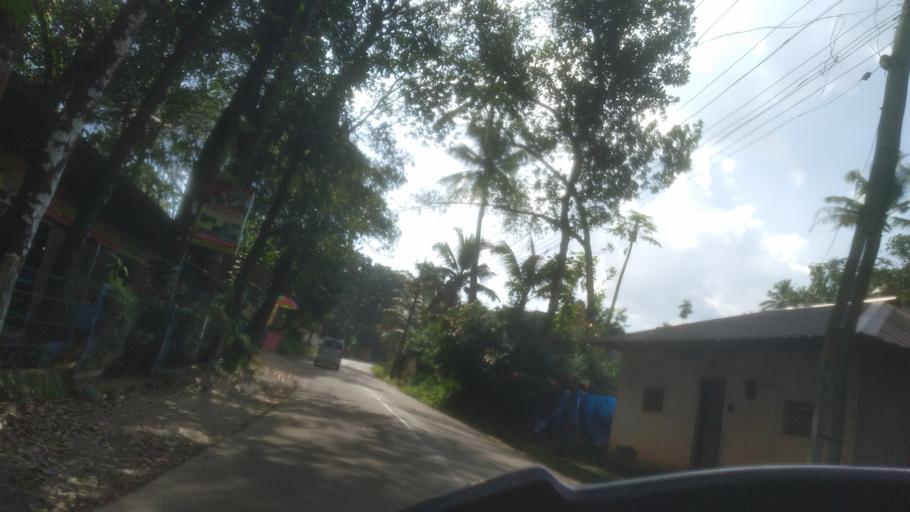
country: IN
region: Kerala
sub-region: Ernakulam
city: Kotamangalam
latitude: 9.9981
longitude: 76.6415
